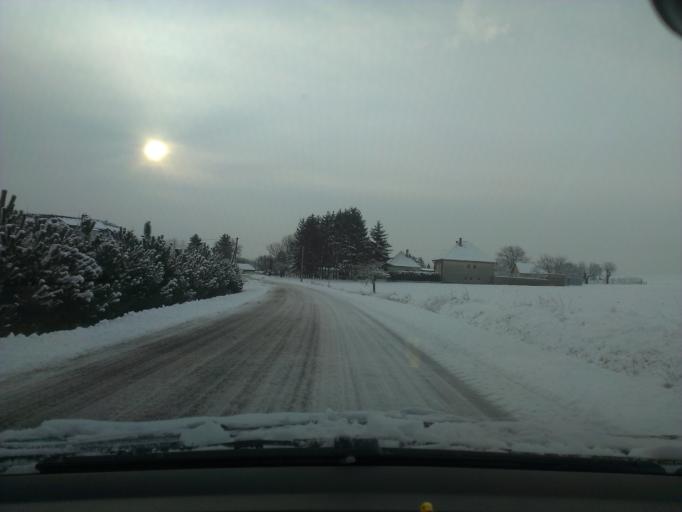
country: SK
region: Trnavsky
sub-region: Okres Trnava
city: Piestany
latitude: 48.5283
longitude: 17.9617
